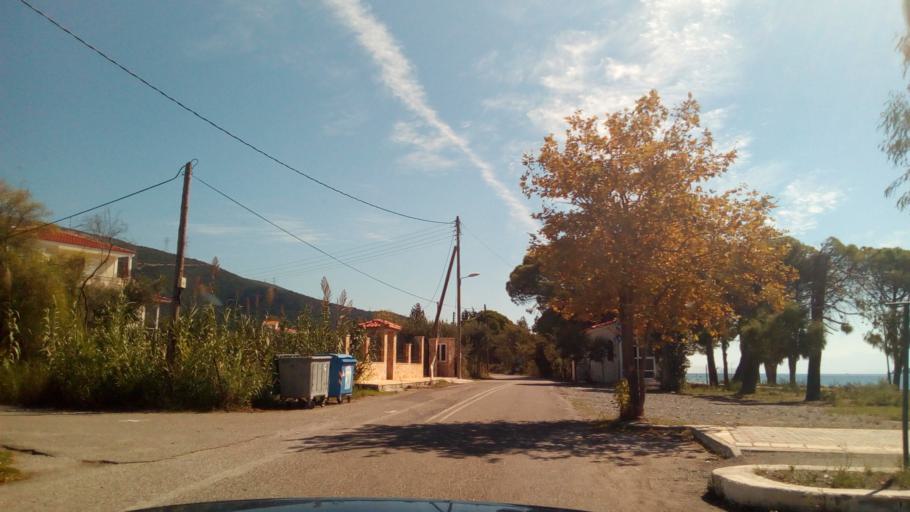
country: GR
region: West Greece
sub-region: Nomos Achaias
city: Selianitika
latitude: 38.3755
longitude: 22.0834
